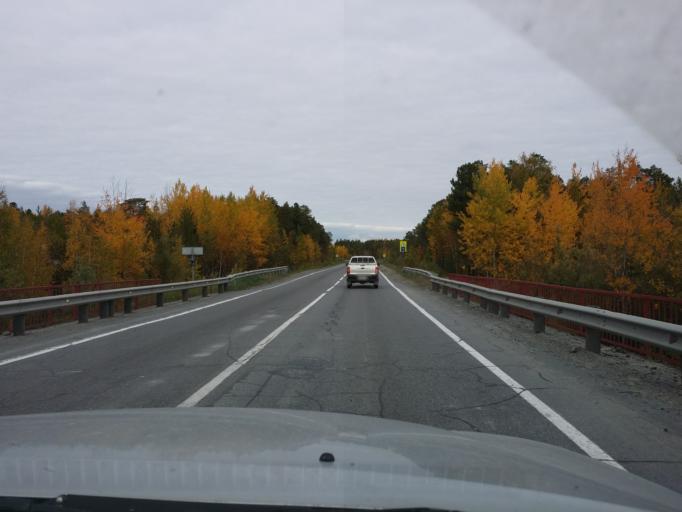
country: RU
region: Khanty-Mansiyskiy Avtonomnyy Okrug
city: Megion
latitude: 61.1187
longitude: 75.8373
